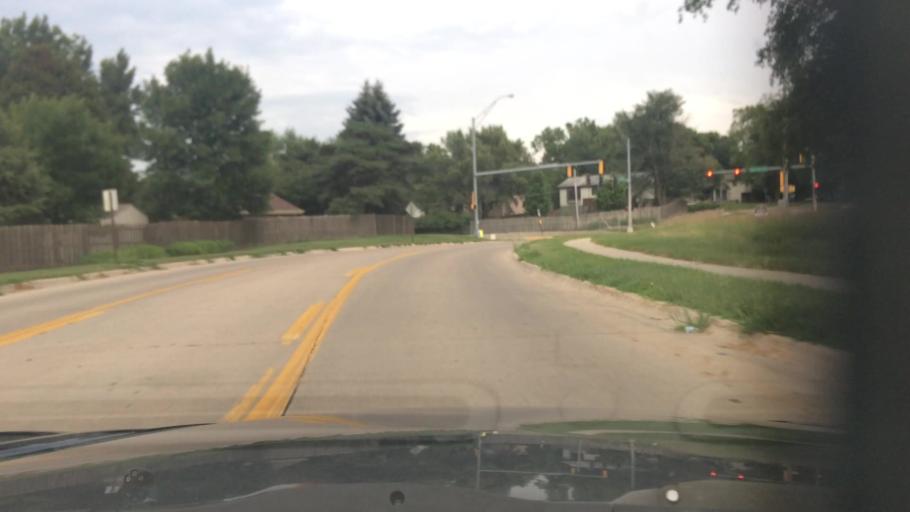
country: US
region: Nebraska
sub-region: Douglas County
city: Ralston
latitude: 41.1915
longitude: -96.0522
